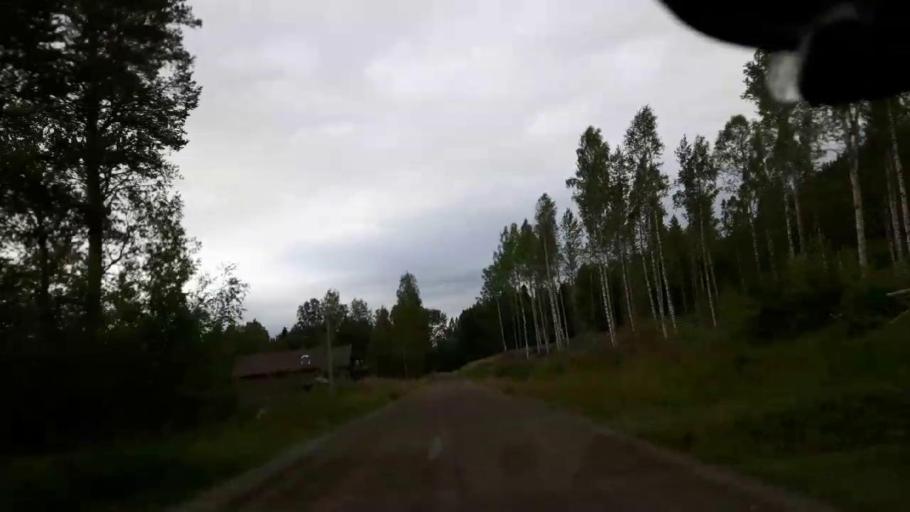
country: SE
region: Jaemtland
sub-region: Braecke Kommun
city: Braecke
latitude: 62.9079
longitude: 15.5912
